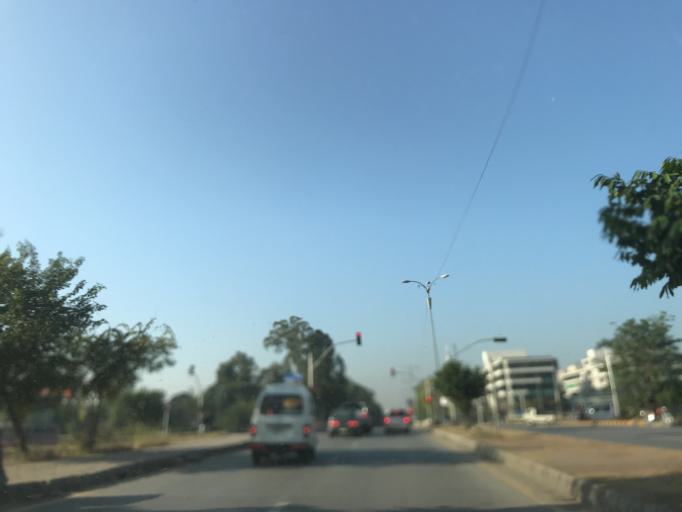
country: PK
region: Islamabad
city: Islamabad
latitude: 33.7175
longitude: 73.0732
